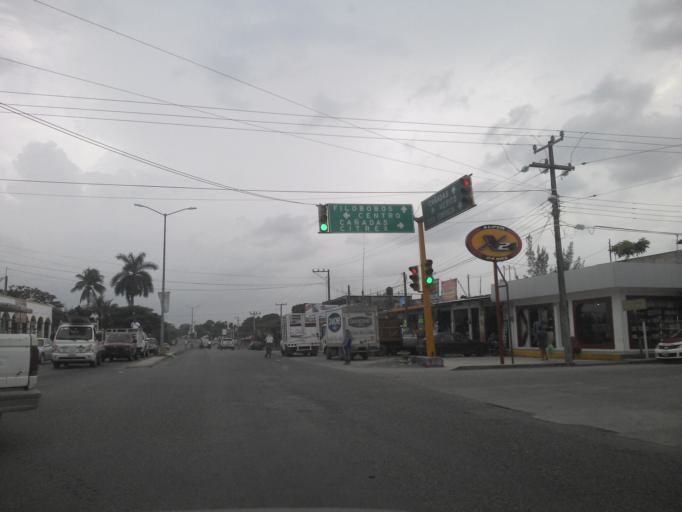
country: MX
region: Veracruz
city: Martinez de la Torre
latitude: 20.0734
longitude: -97.0644
